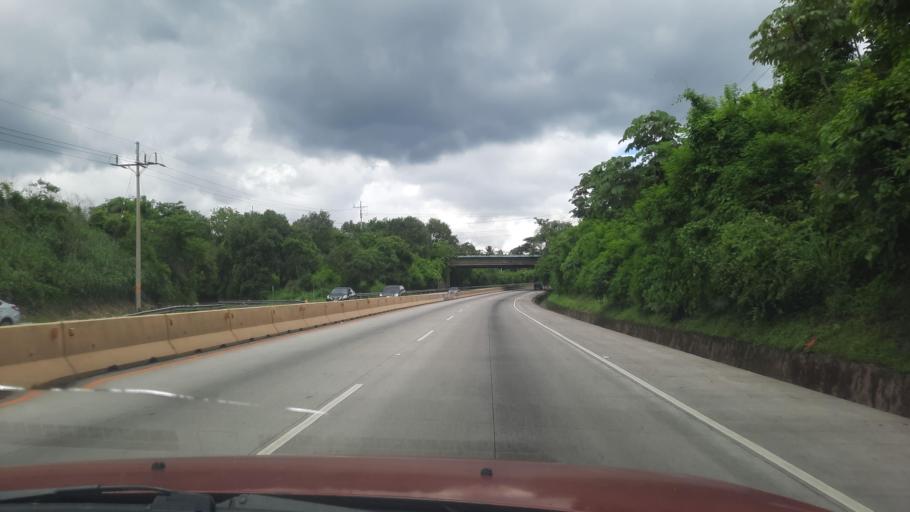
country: SV
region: Sonsonate
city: Sonzacate
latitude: 13.7383
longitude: -89.6965
